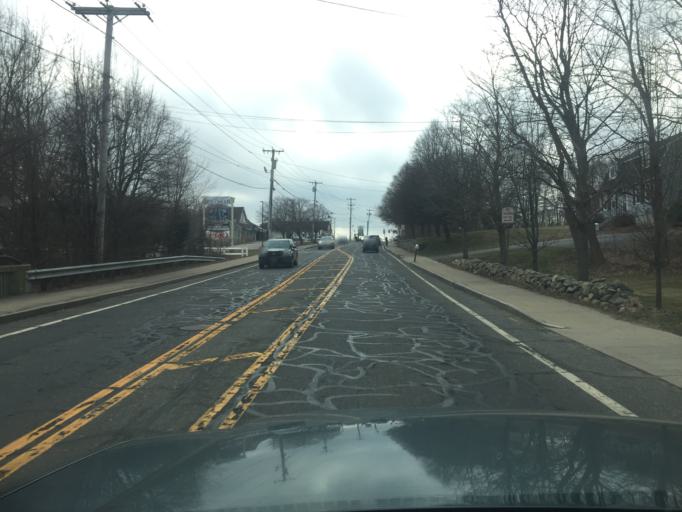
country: US
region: Massachusetts
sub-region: Norfolk County
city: Franklin
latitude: 42.0685
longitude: -71.3967
